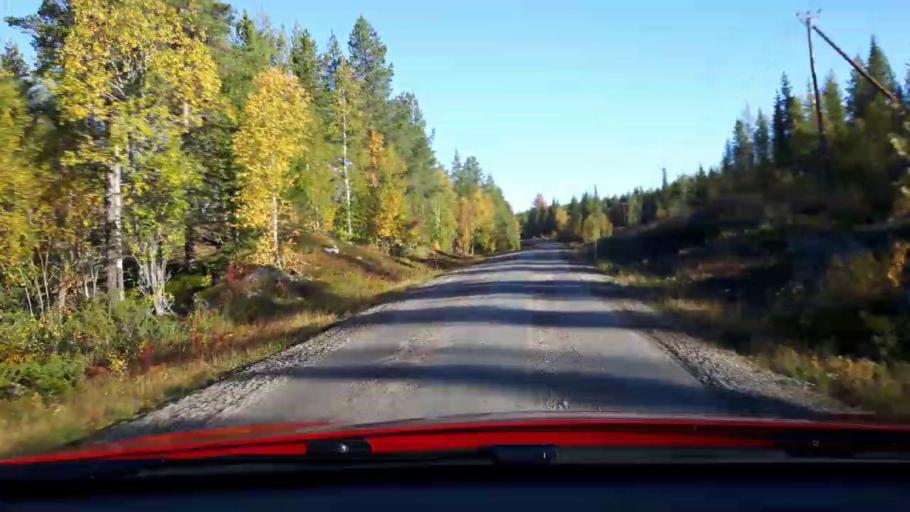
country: SE
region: Jaemtland
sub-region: Stroemsunds Kommun
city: Stroemsund
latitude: 64.3915
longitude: 15.1495
